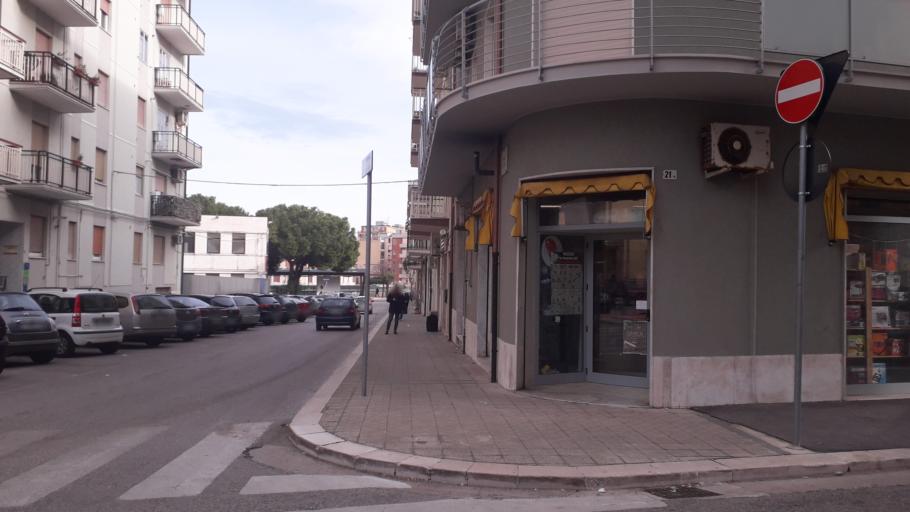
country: IT
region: Molise
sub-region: Provincia di Campobasso
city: Termoli
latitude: 42.0000
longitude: 14.9908
